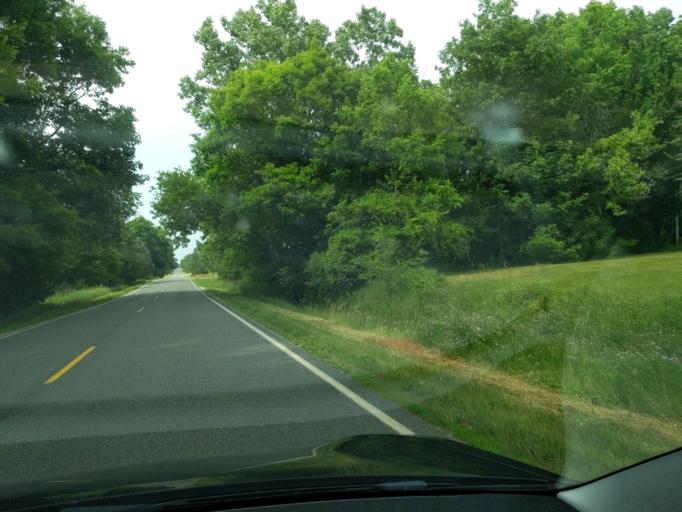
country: US
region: Michigan
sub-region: Clinton County
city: DeWitt
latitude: 42.8778
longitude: -84.6023
